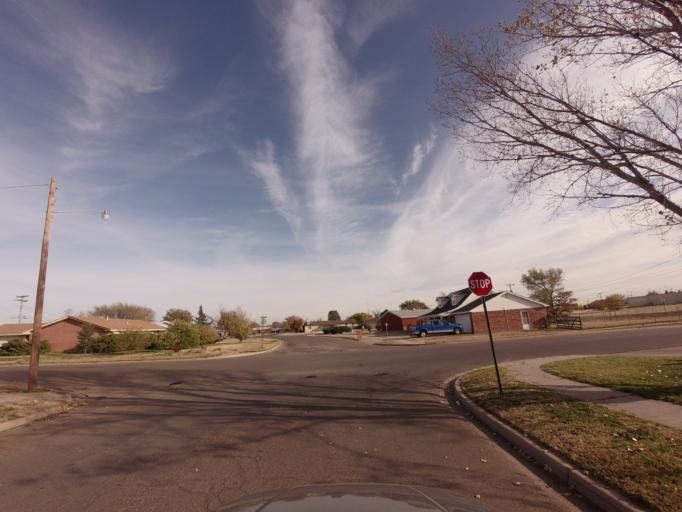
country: US
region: New Mexico
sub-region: Curry County
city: Clovis
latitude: 34.4227
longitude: -103.2199
